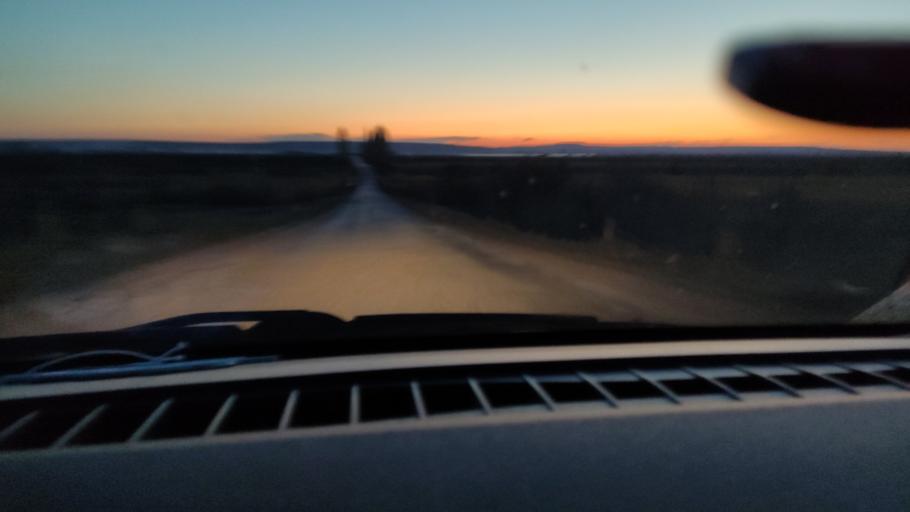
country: RU
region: Saratov
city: Rovnoye
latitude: 50.9390
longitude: 46.1149
